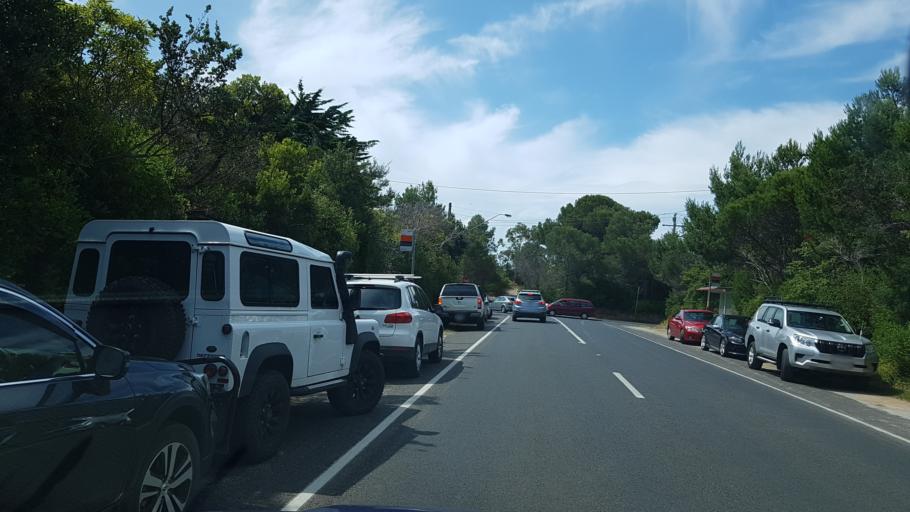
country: AU
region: Victoria
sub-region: Mornington Peninsula
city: Sorrento
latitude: -38.3214
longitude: 144.7182
